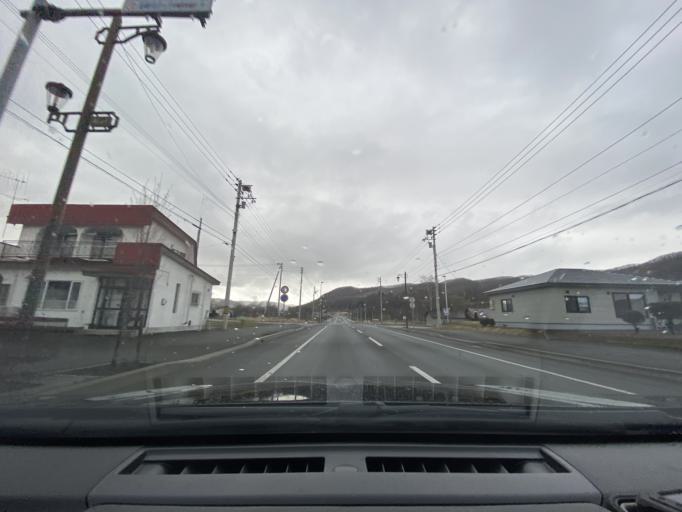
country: JP
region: Hokkaido
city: Otofuke
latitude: 43.2514
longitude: 143.5475
